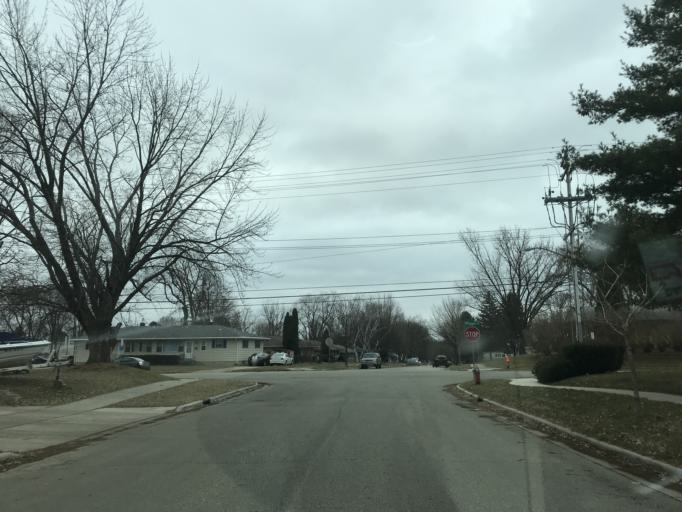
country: US
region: Wisconsin
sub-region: Dane County
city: Monona
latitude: 43.0626
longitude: -89.3118
